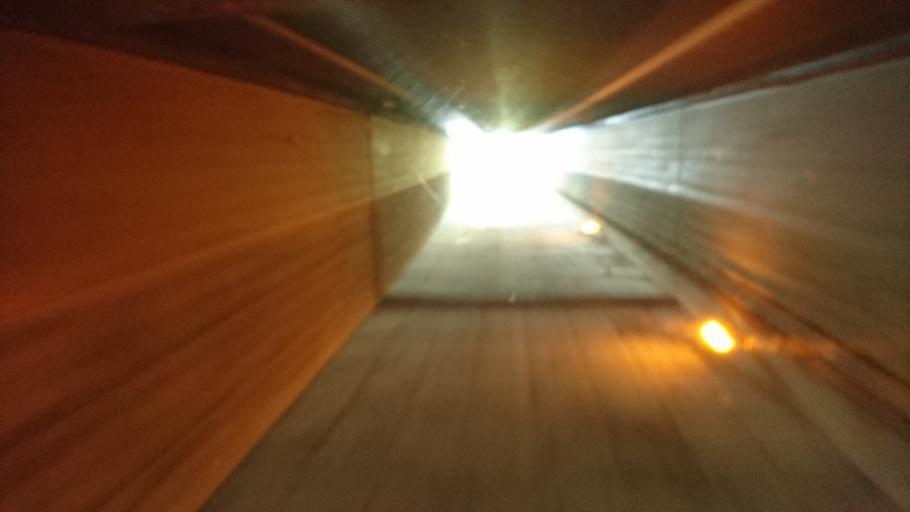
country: JP
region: Iwate
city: Morioka-shi
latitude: 39.7975
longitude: 141.1190
